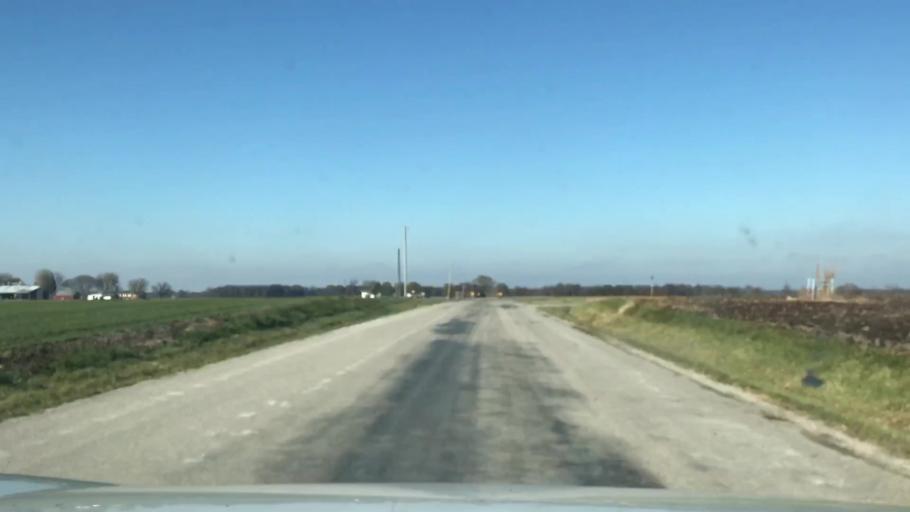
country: US
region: Illinois
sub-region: Washington County
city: Okawville
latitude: 38.4374
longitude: -89.4777
